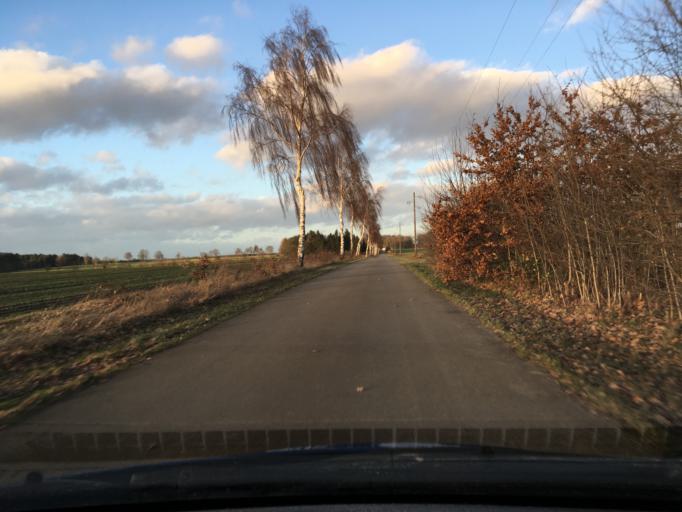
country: DE
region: Lower Saxony
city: Soderstorf
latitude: 53.1171
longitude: 10.1678
